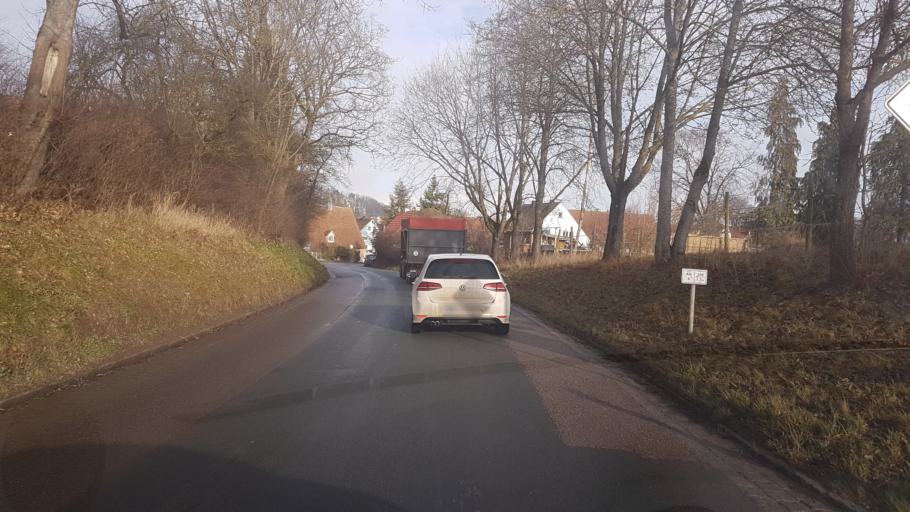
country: DE
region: Bavaria
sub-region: Regierungsbezirk Mittelfranken
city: Dombuhl
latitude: 49.2531
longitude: 10.2814
